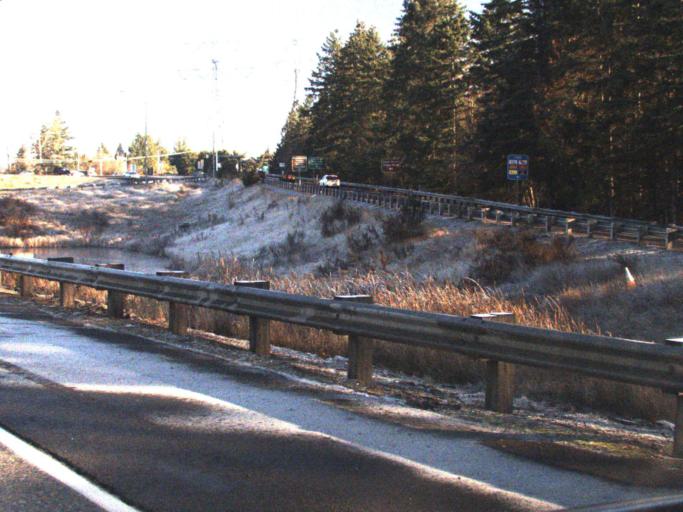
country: US
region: Washington
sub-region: King County
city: Federal Way
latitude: 47.3134
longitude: -122.2979
